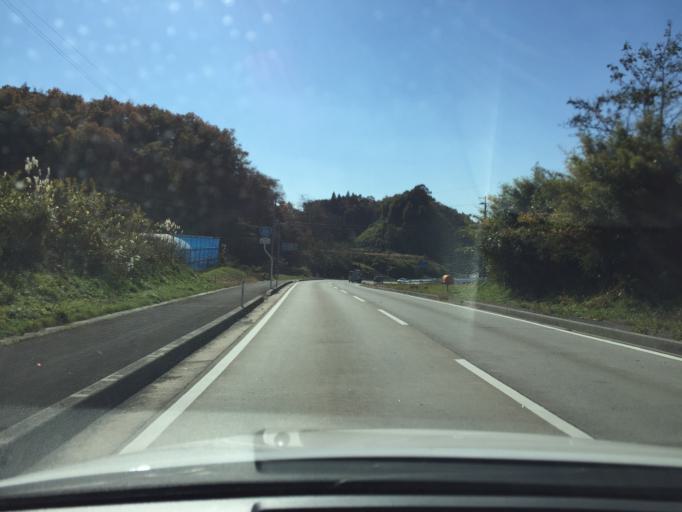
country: JP
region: Fukushima
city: Miharu
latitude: 37.4451
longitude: 140.5125
